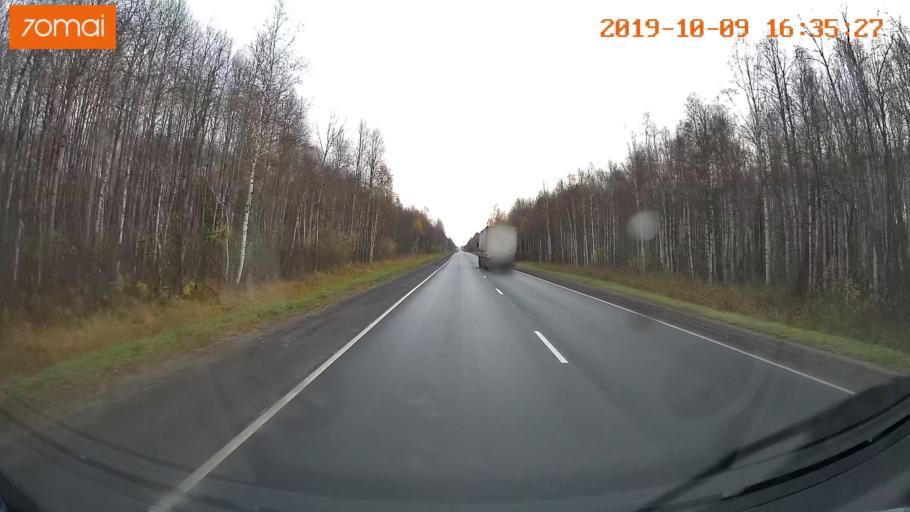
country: RU
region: Kostroma
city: Oktyabr'skiy
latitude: 57.5556
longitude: 41.0010
